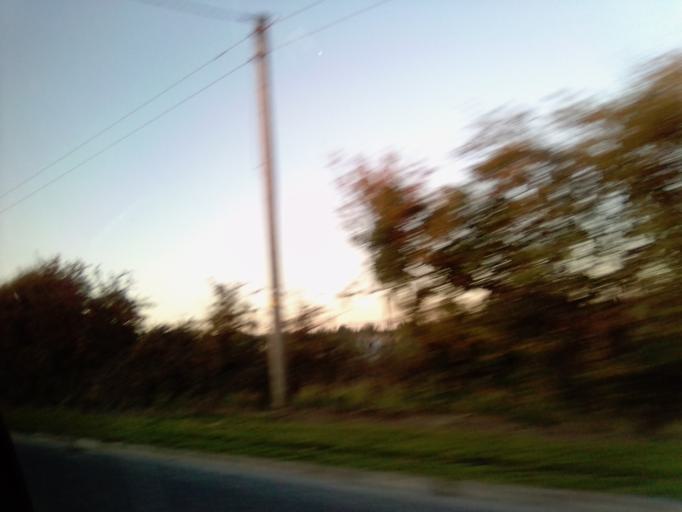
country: IE
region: Leinster
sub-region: Lu
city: Drogheda
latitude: 53.7259
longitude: -6.3825
